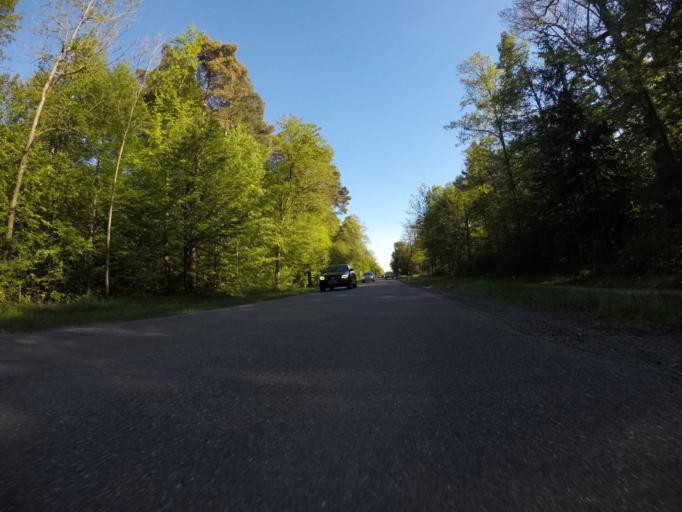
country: DE
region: Baden-Wuerttemberg
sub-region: Regierungsbezirk Stuttgart
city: Gerlingen
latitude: 48.7827
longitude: 9.0904
